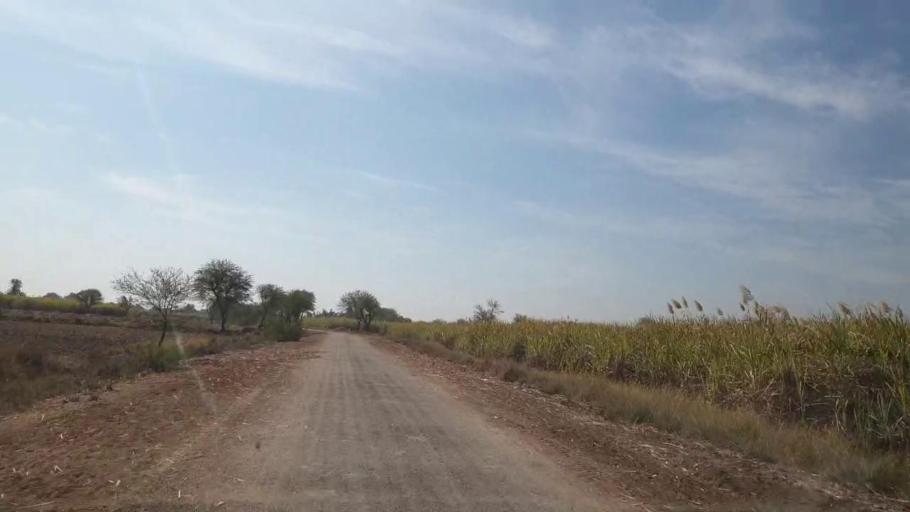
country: PK
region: Sindh
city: Mirpur Khas
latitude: 25.5277
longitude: 69.1452
